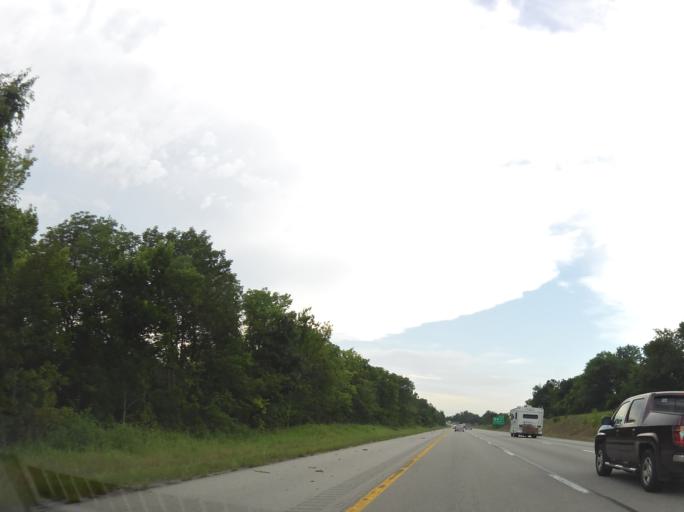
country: US
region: Kentucky
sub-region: Madison County
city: Berea
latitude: 37.6554
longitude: -84.3112
